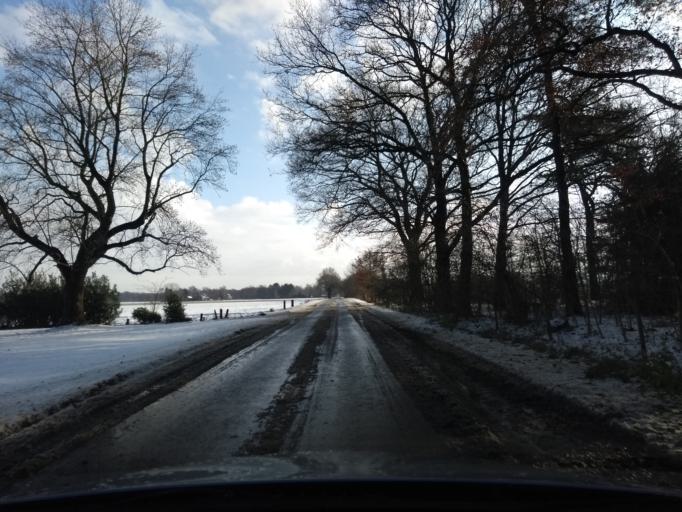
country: NL
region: Gelderland
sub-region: Gemeente Bronckhorst
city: Zelhem
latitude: 52.0345
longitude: 6.3438
